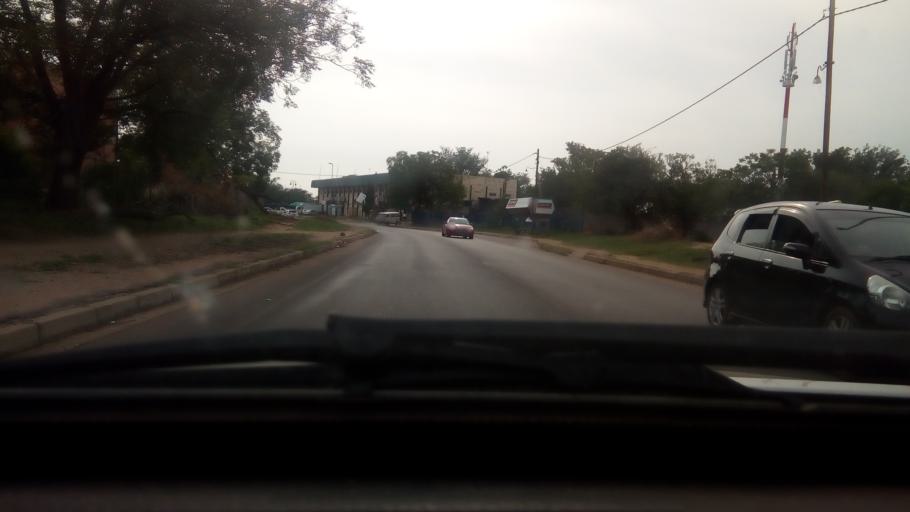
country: BW
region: South East
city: Gaborone
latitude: -24.6674
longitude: 25.9385
